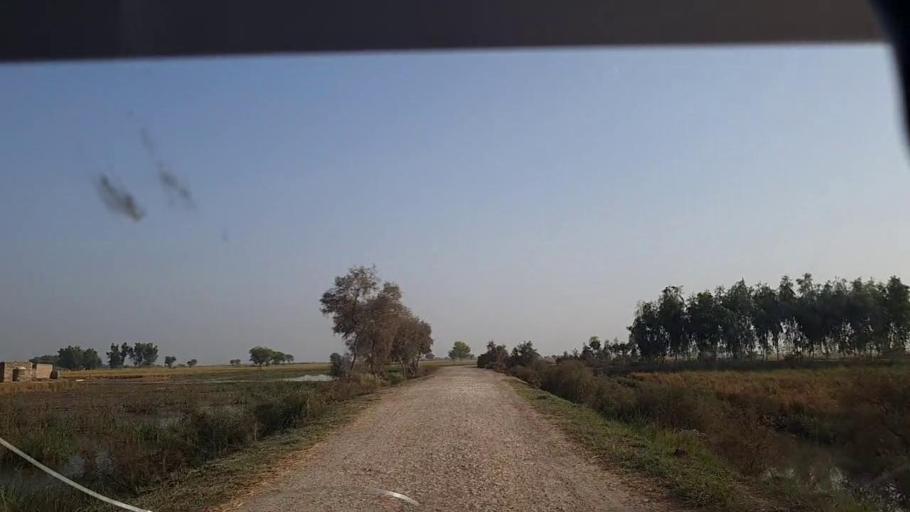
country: PK
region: Sindh
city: Shikarpur
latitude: 28.0636
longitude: 68.5480
